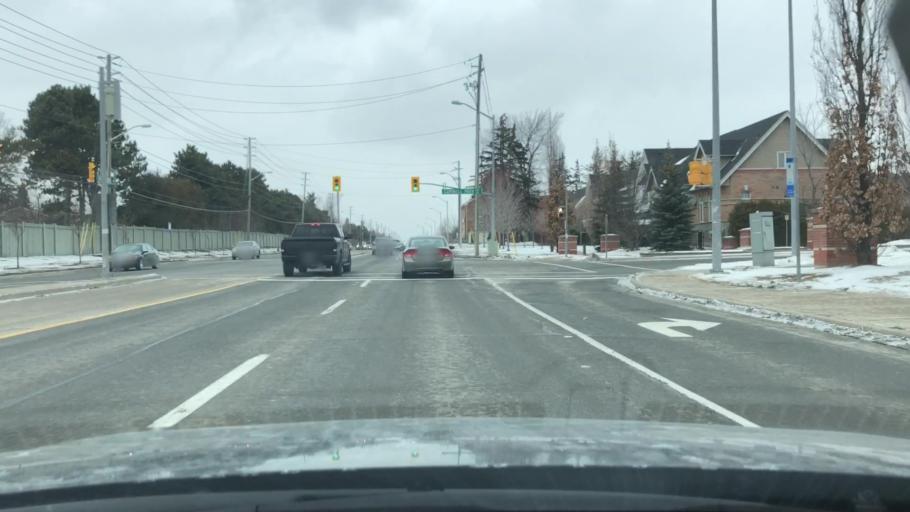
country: CA
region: Ontario
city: Markham
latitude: 43.8882
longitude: -79.2371
